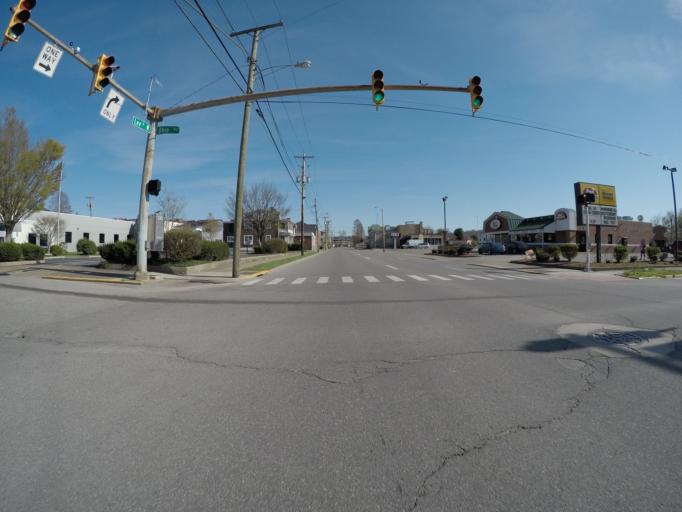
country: US
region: West Virginia
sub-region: Kanawha County
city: Charleston
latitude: 38.3615
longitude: -81.6433
